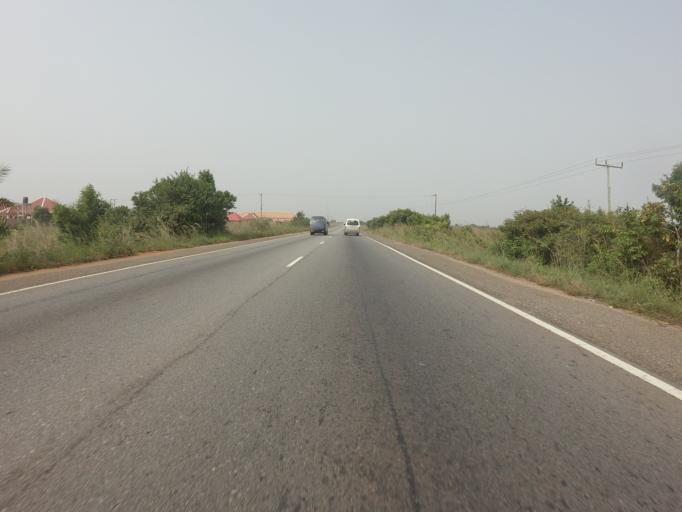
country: GH
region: Volta
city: Anloga
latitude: 5.9260
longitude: 0.5232
